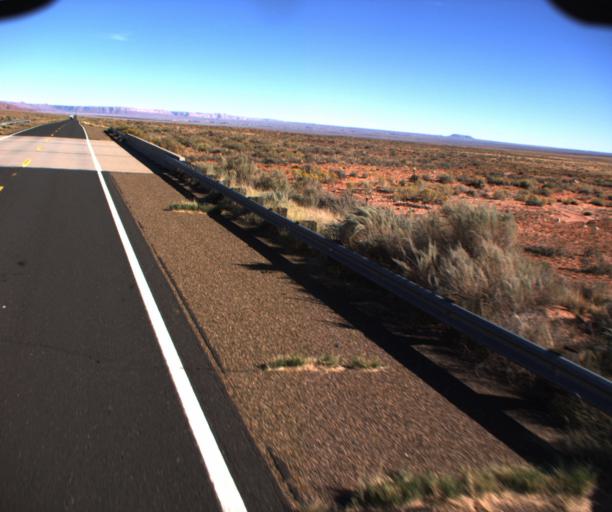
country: US
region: Arizona
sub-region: Coconino County
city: Fredonia
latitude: 36.7171
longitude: -111.9996
